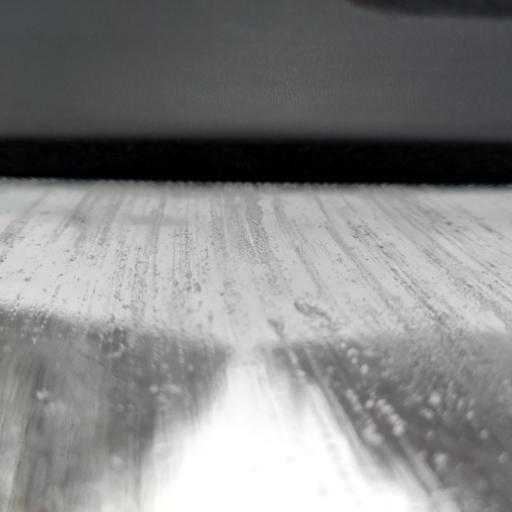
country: RU
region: Perm
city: Polazna
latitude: 58.1429
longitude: 56.4326
